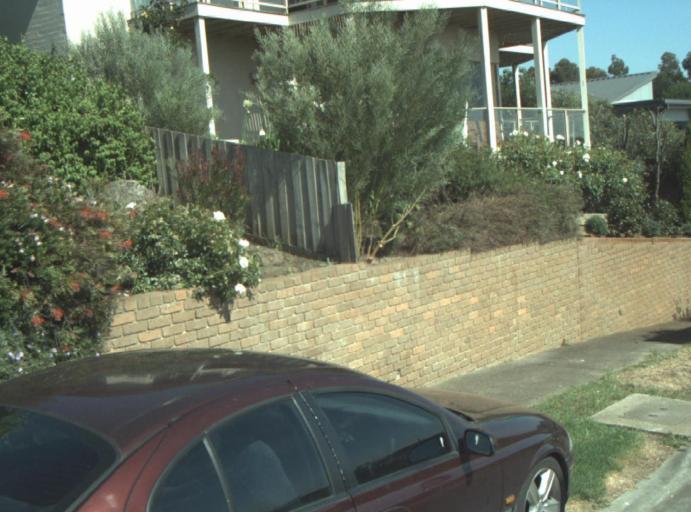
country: AU
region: Victoria
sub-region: Greater Geelong
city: Wandana Heights
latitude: -38.1606
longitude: 144.3149
